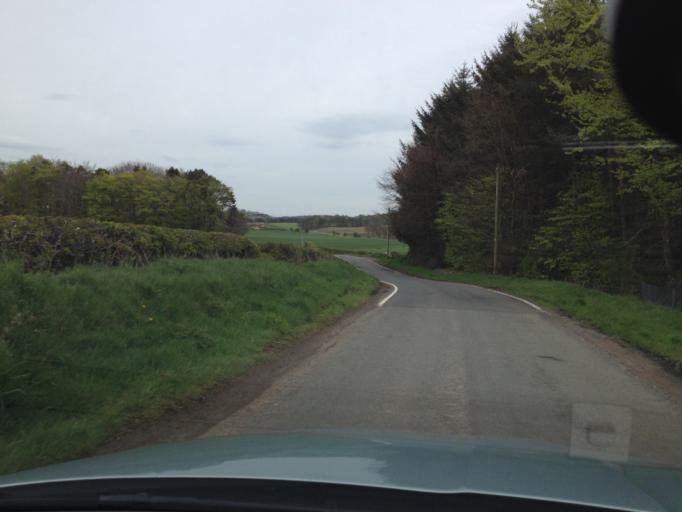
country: GB
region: Scotland
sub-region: West Lothian
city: Linlithgow
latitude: 55.9359
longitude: -3.5926
